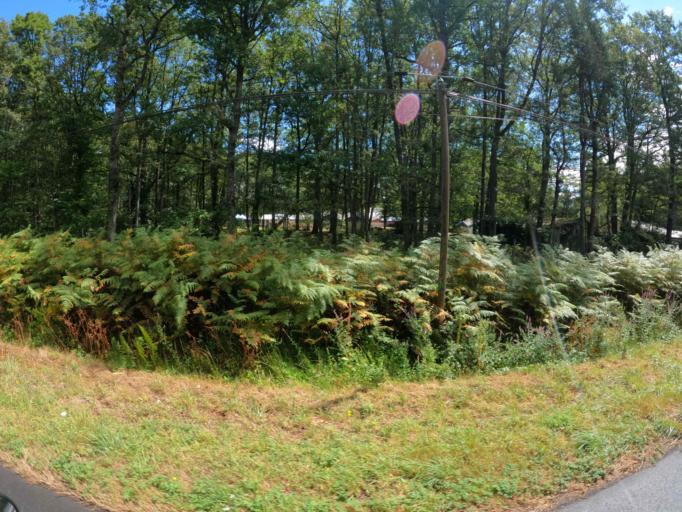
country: FR
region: Pays de la Loire
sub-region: Departement de Maine-et-Loire
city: Feneu
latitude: 47.5819
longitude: -0.5915
